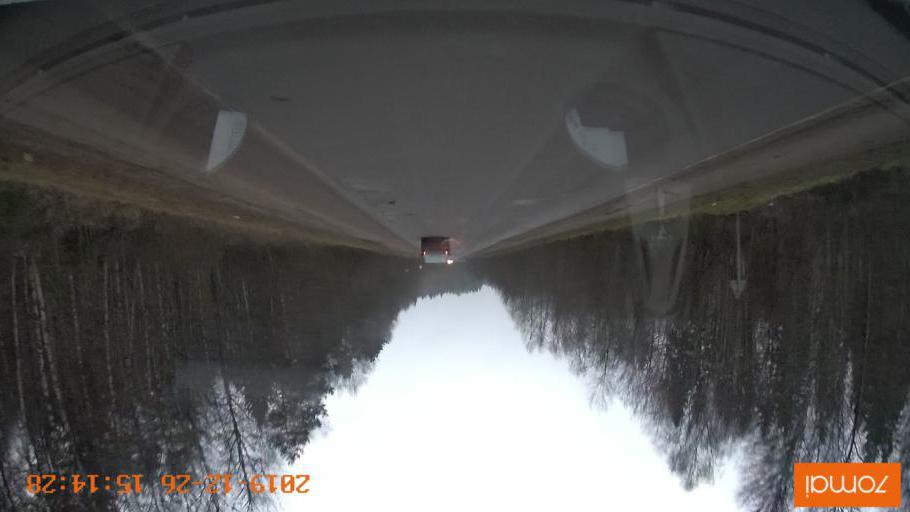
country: RU
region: Jaroslavl
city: Rybinsk
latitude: 58.1057
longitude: 38.8800
